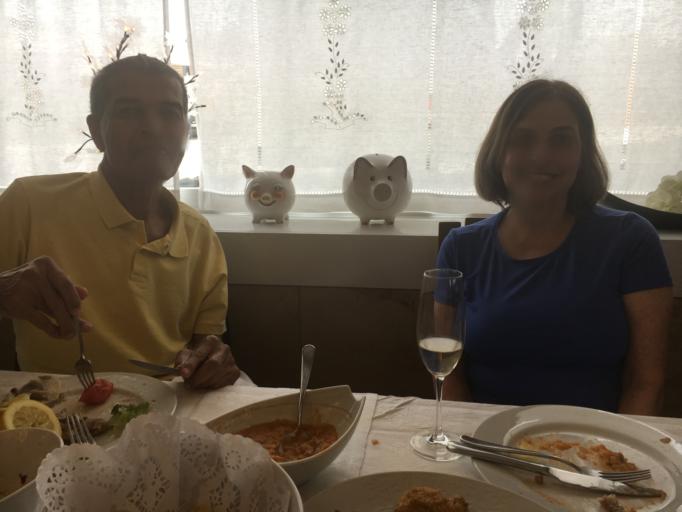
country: PT
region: Aveiro
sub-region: Mealhada
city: Mealhada
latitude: 40.3903
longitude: -8.4506
